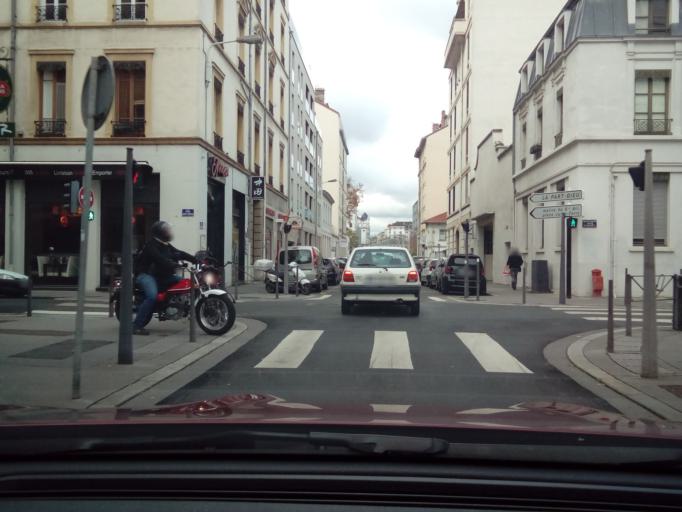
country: FR
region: Rhone-Alpes
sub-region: Departement du Rhone
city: Villeurbanne
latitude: 45.7664
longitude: 4.8651
